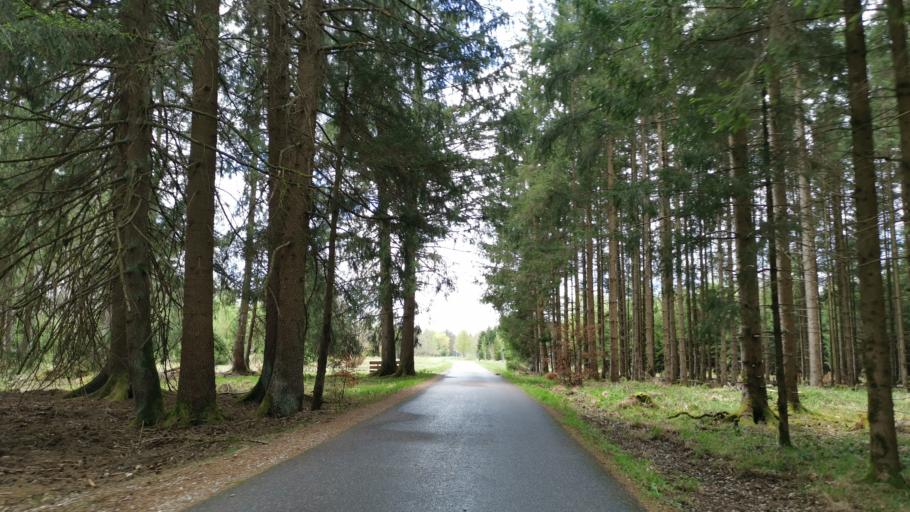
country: DE
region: Bavaria
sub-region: Upper Bavaria
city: Baierbrunn
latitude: 48.0563
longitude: 11.4855
